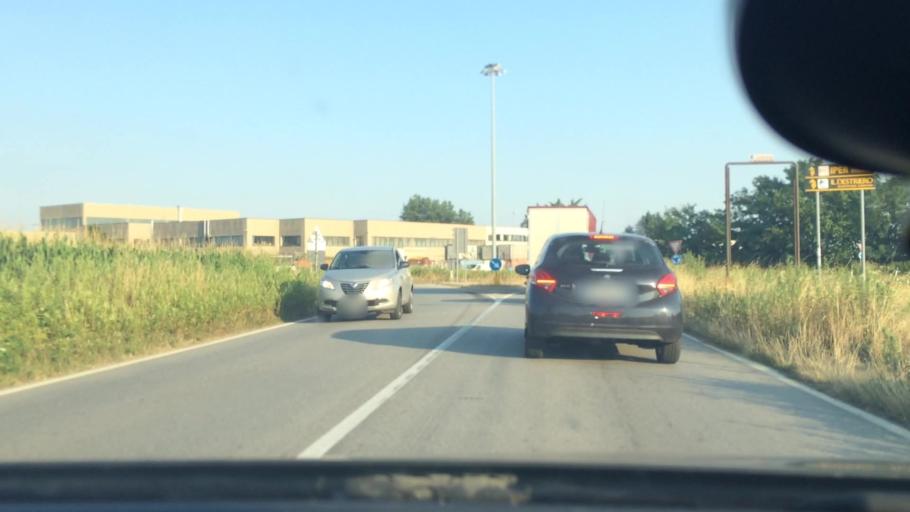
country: IT
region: Lombardy
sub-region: Citta metropolitana di Milano
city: Mantegazza
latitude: 45.5087
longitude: 8.9629
